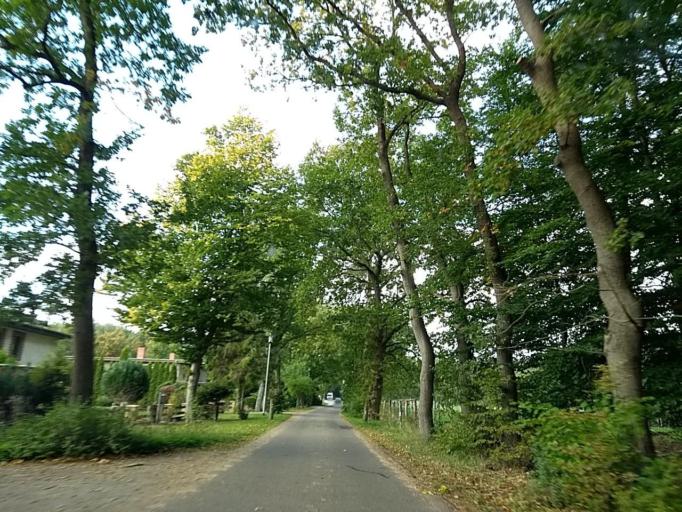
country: DE
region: Mecklenburg-Vorpommern
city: Rovershagen
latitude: 54.1838
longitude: 12.2486
